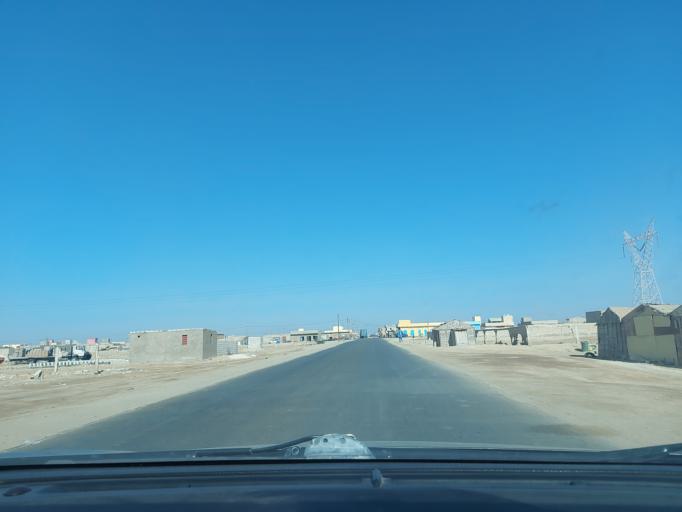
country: MR
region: Nouakchott
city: Nouakchott
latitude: 18.0115
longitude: -15.9858
